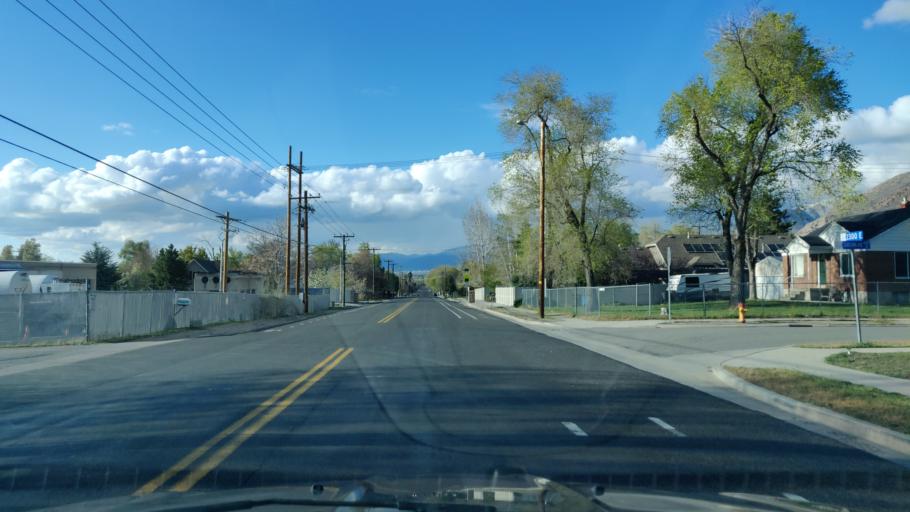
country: US
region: Utah
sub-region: Salt Lake County
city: Cottonwood Heights
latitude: 40.6269
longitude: -111.8247
